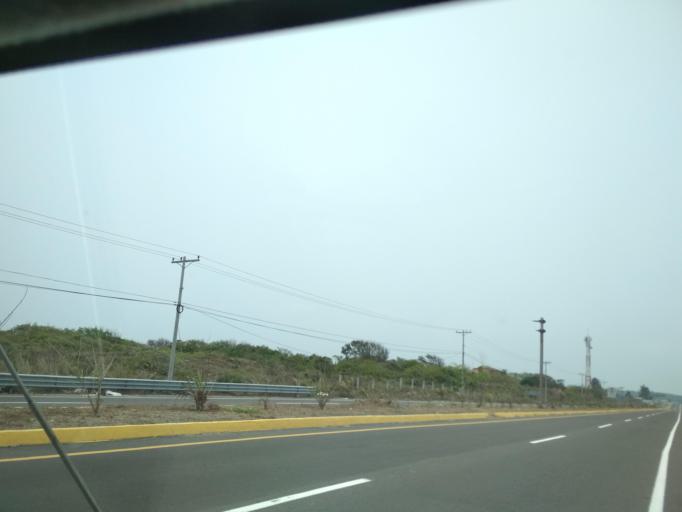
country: MX
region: Veracruz
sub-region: Alvarado
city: Playa de la Libertad
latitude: 19.0558
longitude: -96.0517
